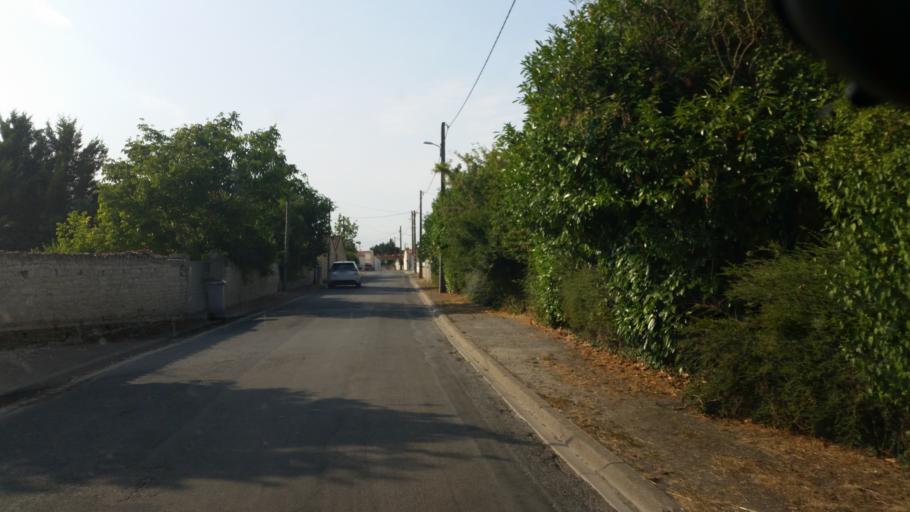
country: FR
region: Poitou-Charentes
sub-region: Departement de la Charente-Maritime
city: Saint-Jean-de-Liversay
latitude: 46.3008
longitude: -0.8935
